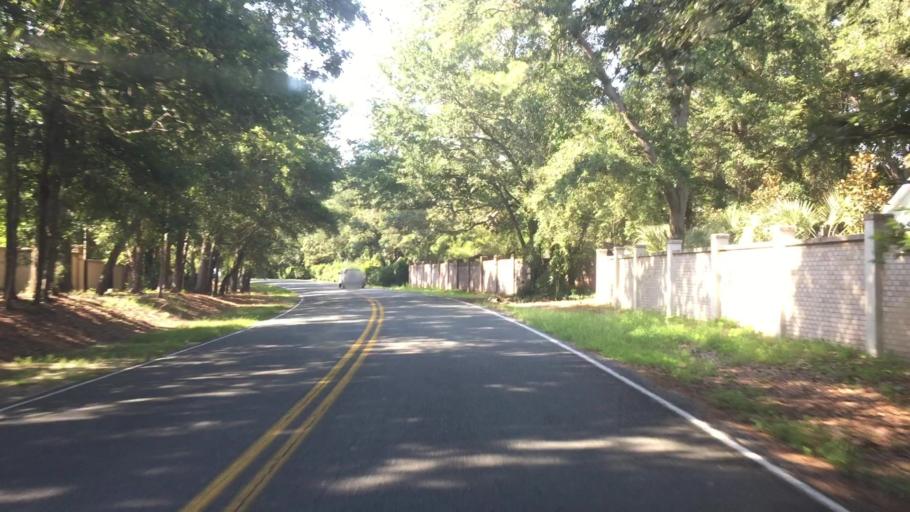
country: US
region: South Carolina
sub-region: Horry County
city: Myrtle Beach
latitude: 33.7544
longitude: -78.8058
